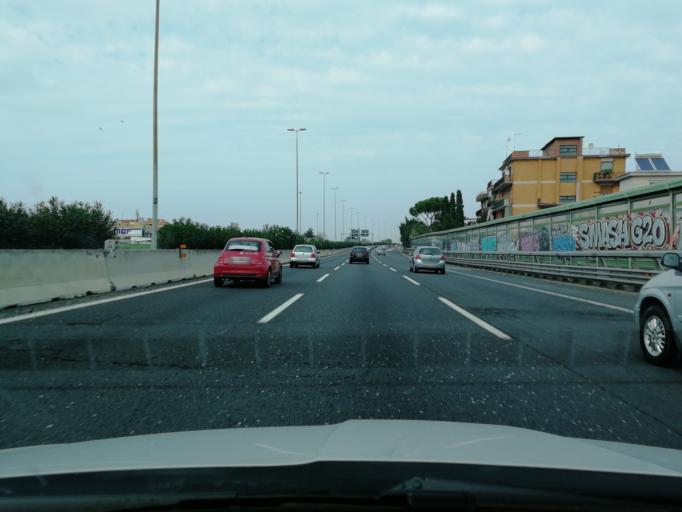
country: IT
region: Latium
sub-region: Citta metropolitana di Roma Capitale
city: Ciampino
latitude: 41.8607
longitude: 12.5997
